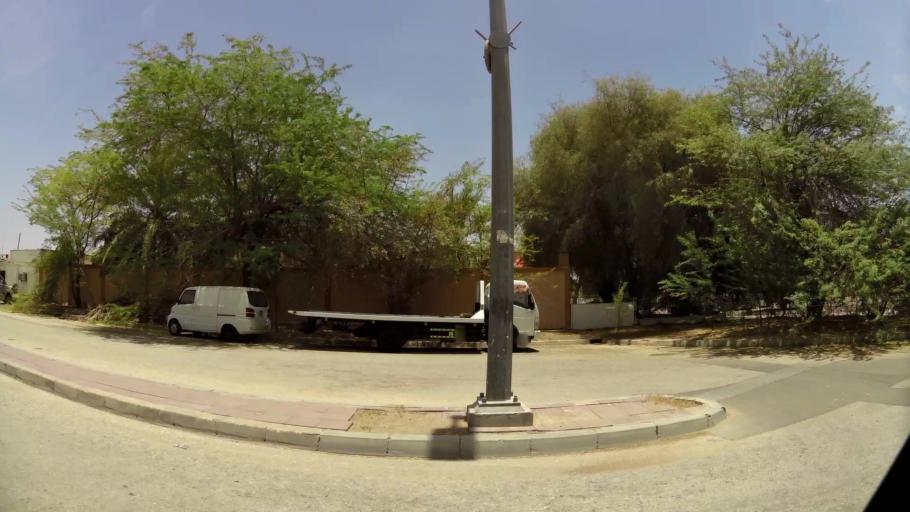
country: OM
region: Al Buraimi
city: Al Buraymi
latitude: 24.2624
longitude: 55.7329
